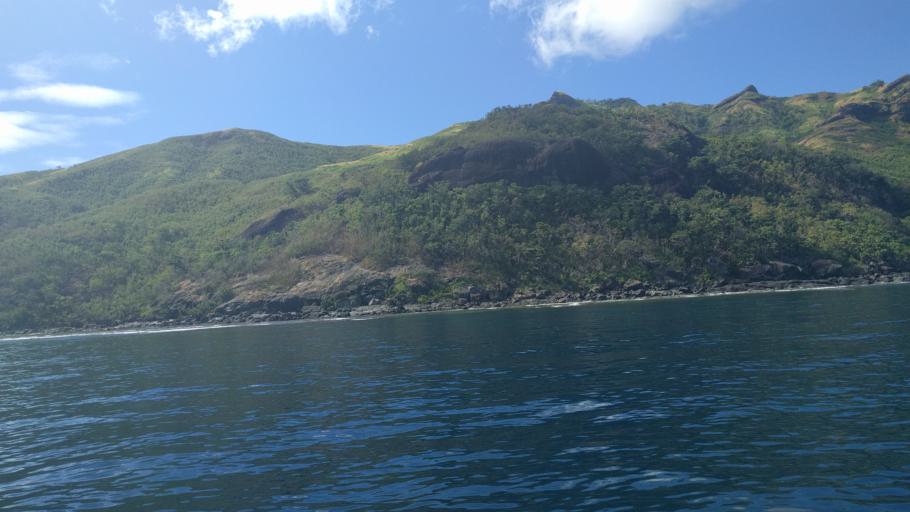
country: FJ
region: Western
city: Lautoka
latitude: -17.2882
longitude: 177.1009
